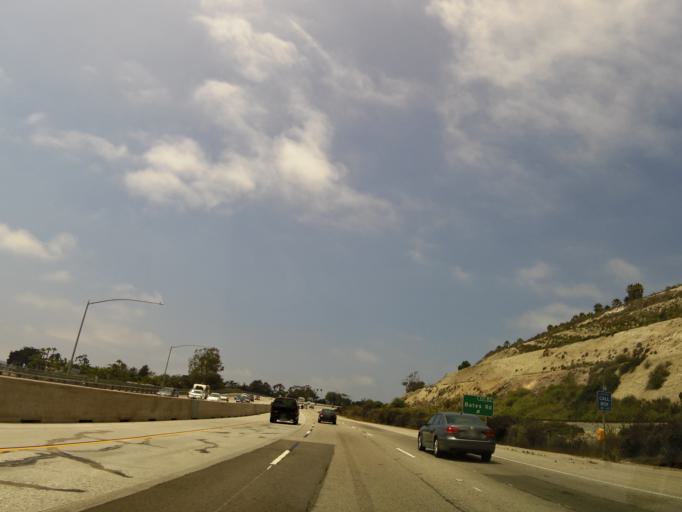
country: US
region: California
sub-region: Santa Barbara County
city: Carpinteria
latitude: 34.3764
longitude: -119.4713
